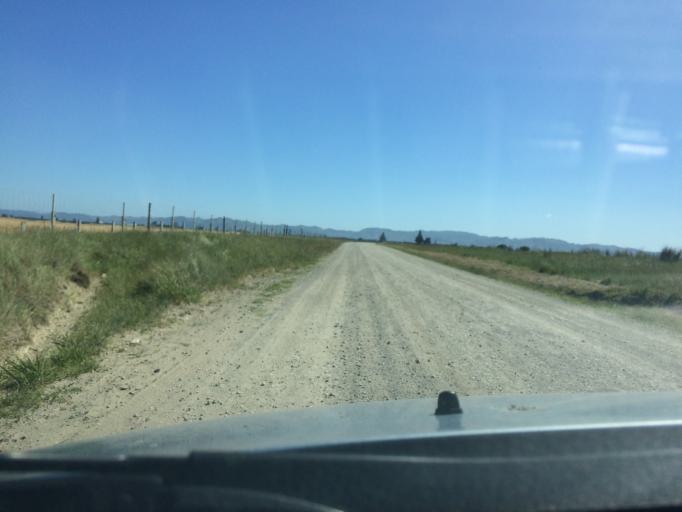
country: NZ
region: Gisborne
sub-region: Gisborne District
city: Gisborne
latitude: -38.7024
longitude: 177.9475
